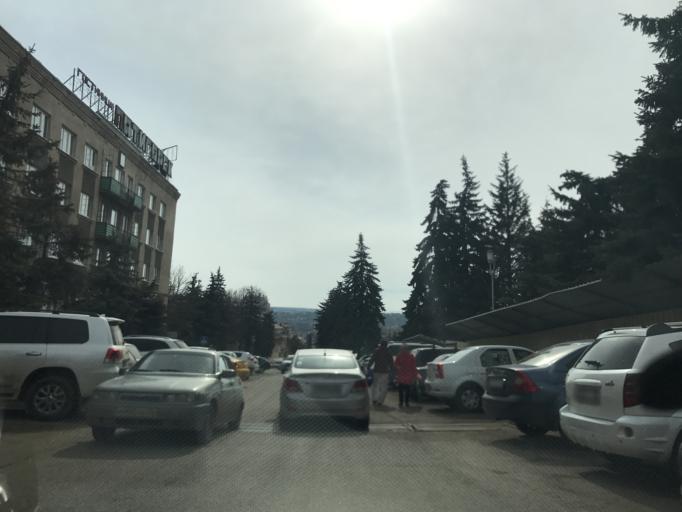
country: RU
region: Stavropol'skiy
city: Pyatigorsk
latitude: 44.0409
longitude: 43.0708
